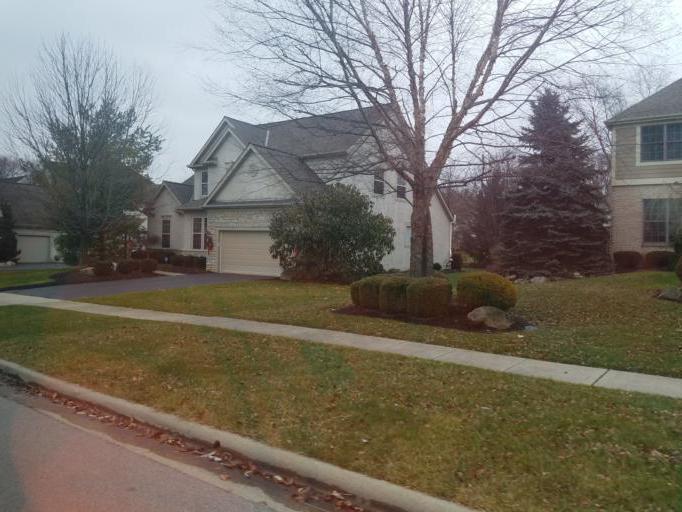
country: US
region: Ohio
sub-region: Franklin County
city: Westerville
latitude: 40.1744
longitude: -82.9396
